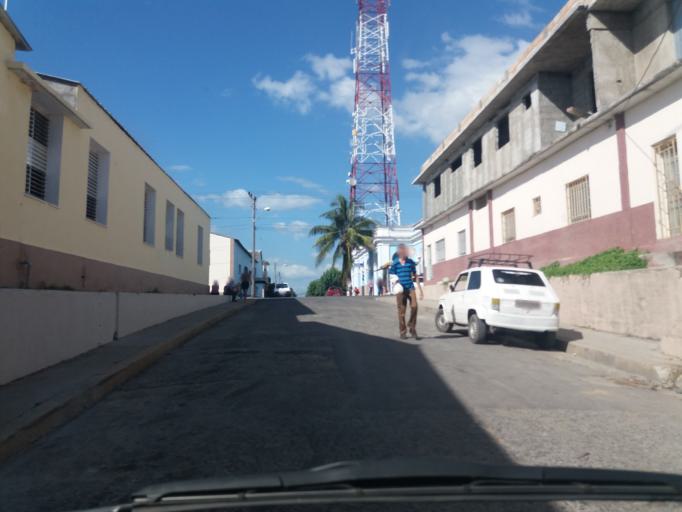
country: CU
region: Cienfuegos
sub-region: Municipio de Cienfuegos
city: Cienfuegos
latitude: 22.1461
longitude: -80.4453
